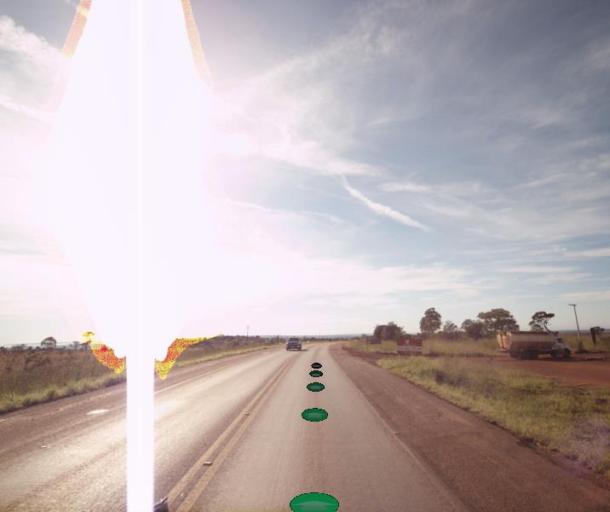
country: BR
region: Federal District
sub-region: Brasilia
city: Brasilia
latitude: -15.7382
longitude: -48.3899
